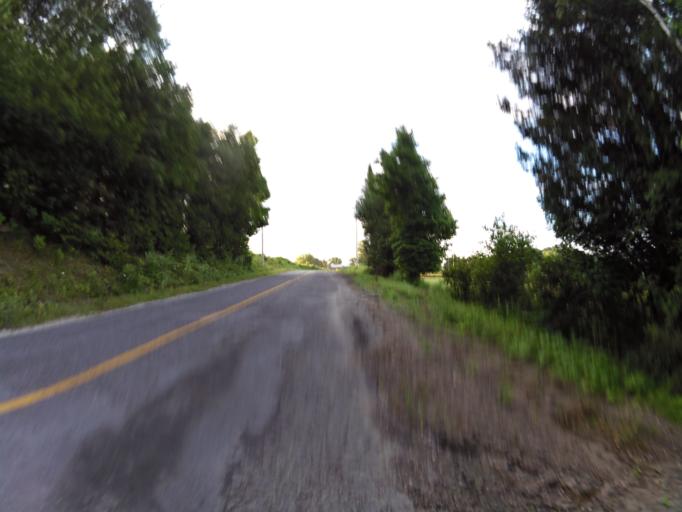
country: CA
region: Quebec
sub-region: Outaouais
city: Wakefield
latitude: 45.7181
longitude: -75.9631
